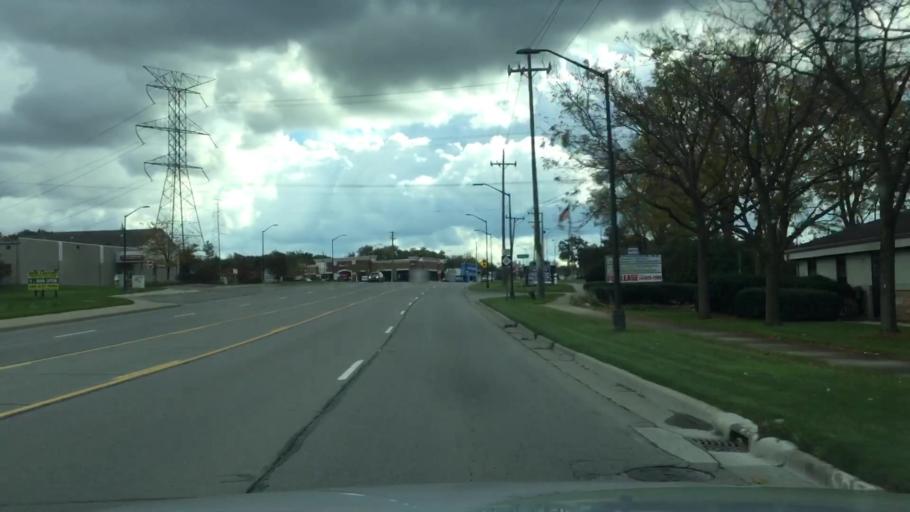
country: US
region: Michigan
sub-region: Oakland County
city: Clarkston
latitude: 42.7221
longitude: -83.4216
